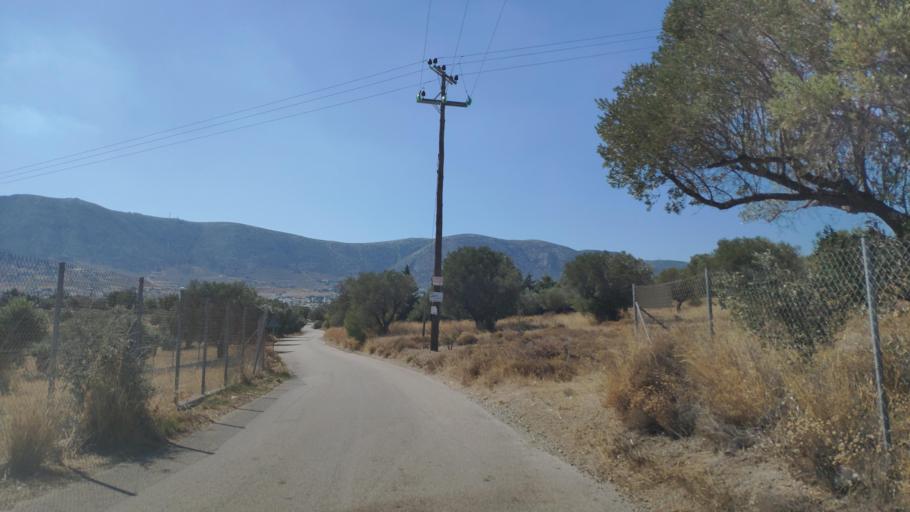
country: GR
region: Attica
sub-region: Nomarchia Anatolikis Attikis
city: Keratea
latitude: 37.8171
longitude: 23.9904
